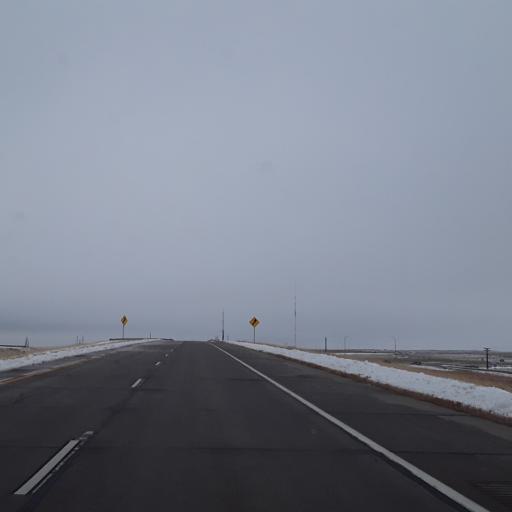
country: US
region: Colorado
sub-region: Logan County
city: Sterling
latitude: 40.6188
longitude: -103.1736
